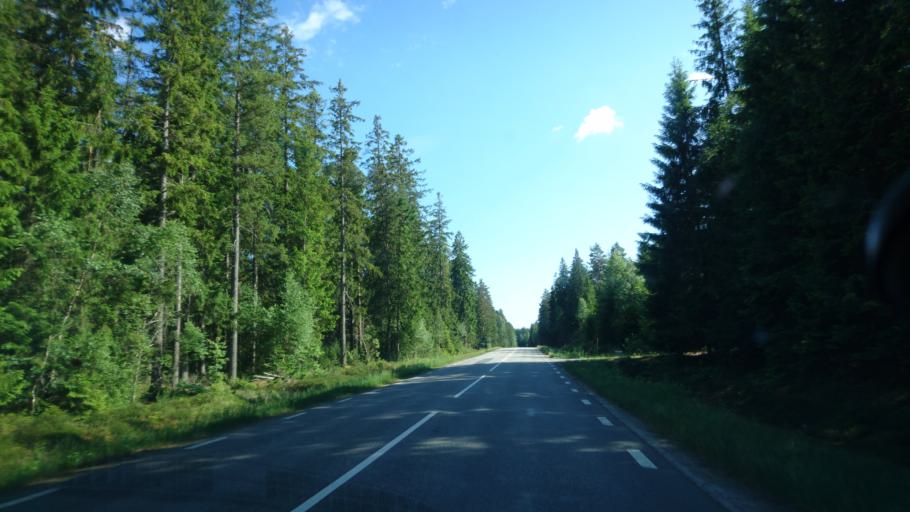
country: SE
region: Skane
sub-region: Osby Kommun
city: Lonsboda
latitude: 56.4609
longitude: 14.2334
